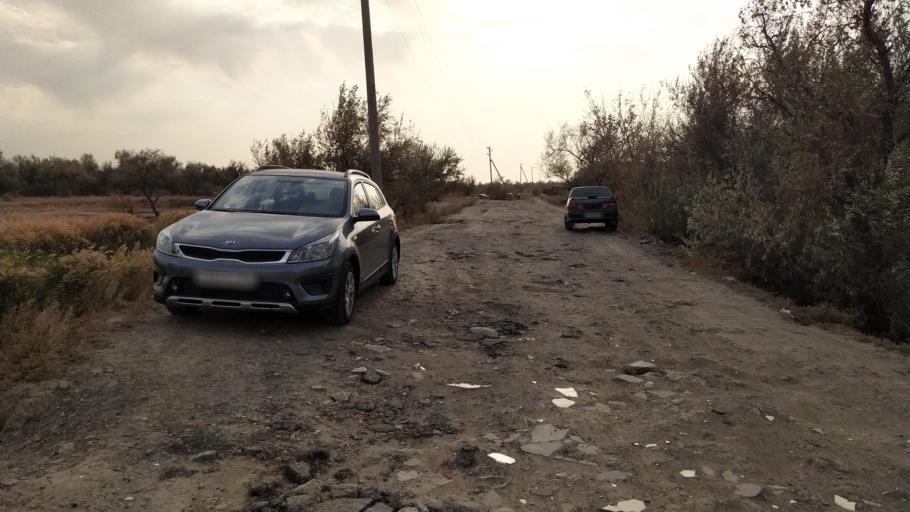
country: RU
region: Rostov
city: Kuleshovka
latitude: 47.1420
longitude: 39.5793
